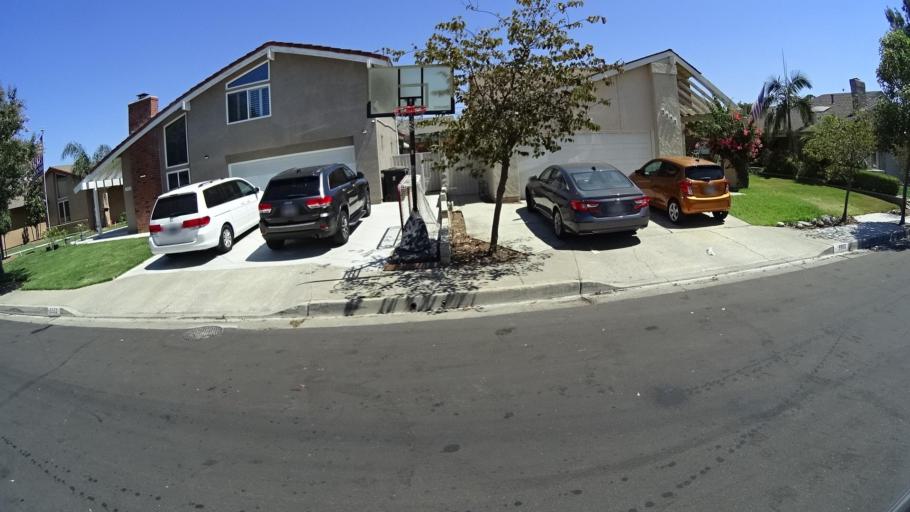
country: US
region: California
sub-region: Orange County
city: Yorba Linda
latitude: 33.8805
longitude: -117.7915
